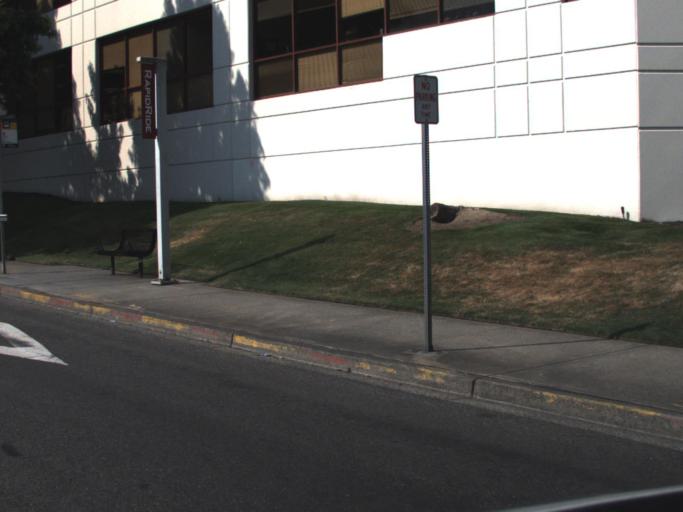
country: US
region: Washington
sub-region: King County
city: SeaTac
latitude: 47.4275
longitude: -122.2958
